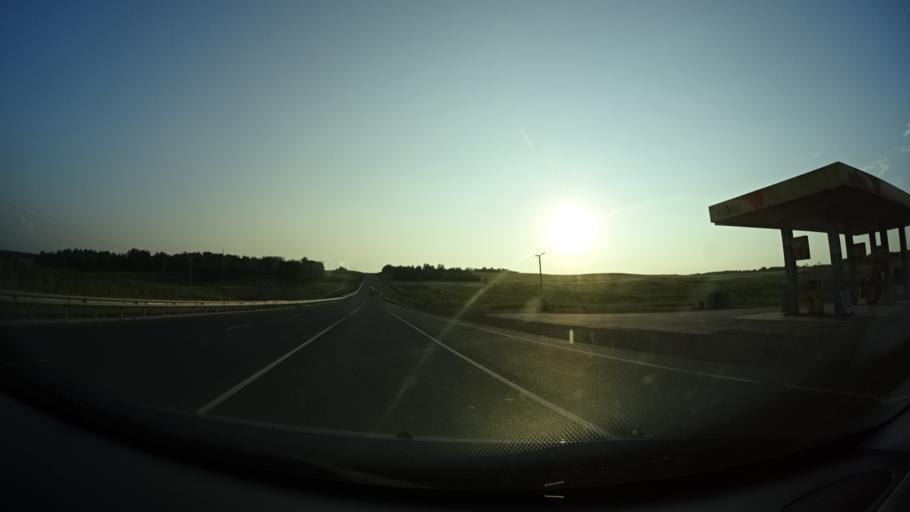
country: RU
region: Samara
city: Isakly
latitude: 54.0179
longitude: 51.7816
